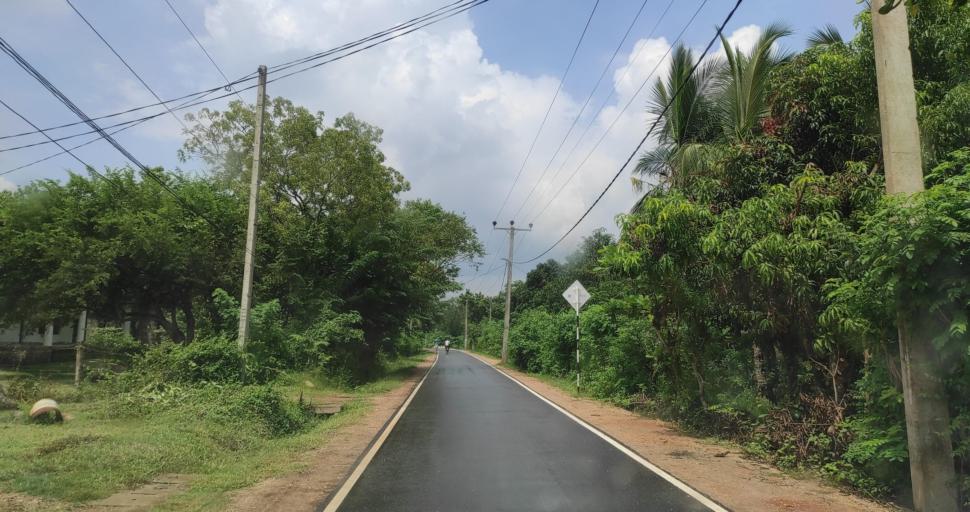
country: LK
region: Eastern Province
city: Trincomalee
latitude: 8.3726
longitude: 81.0115
